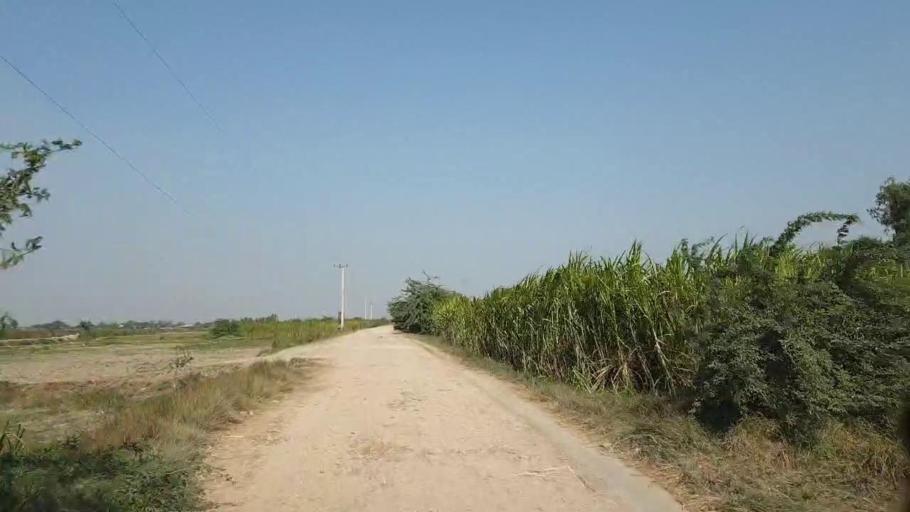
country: PK
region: Sindh
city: Bulri
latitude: 24.9357
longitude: 68.3843
